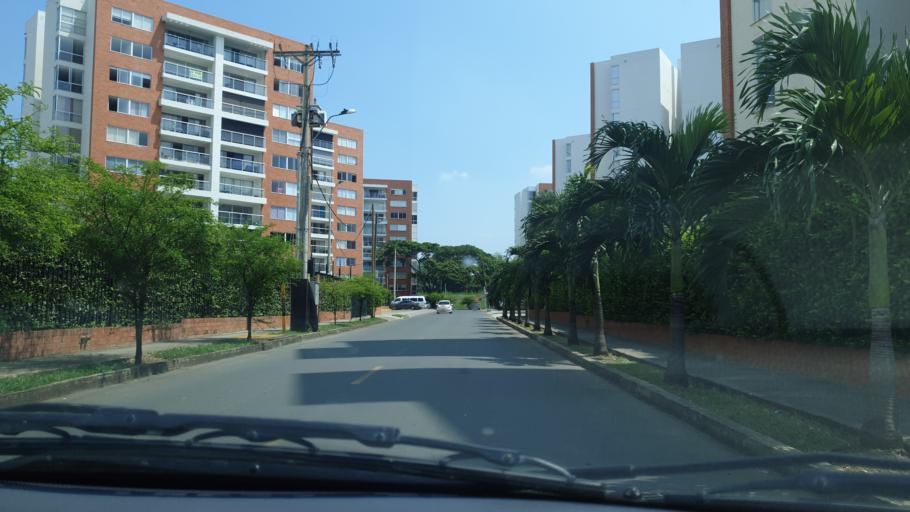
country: CO
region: Valle del Cauca
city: Cali
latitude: 3.3660
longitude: -76.5217
